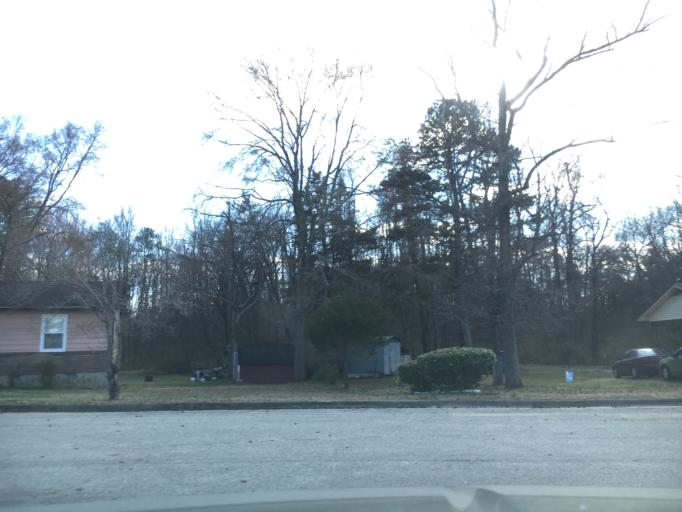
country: US
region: Virginia
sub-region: Halifax County
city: South Boston
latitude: 36.7137
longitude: -78.8927
